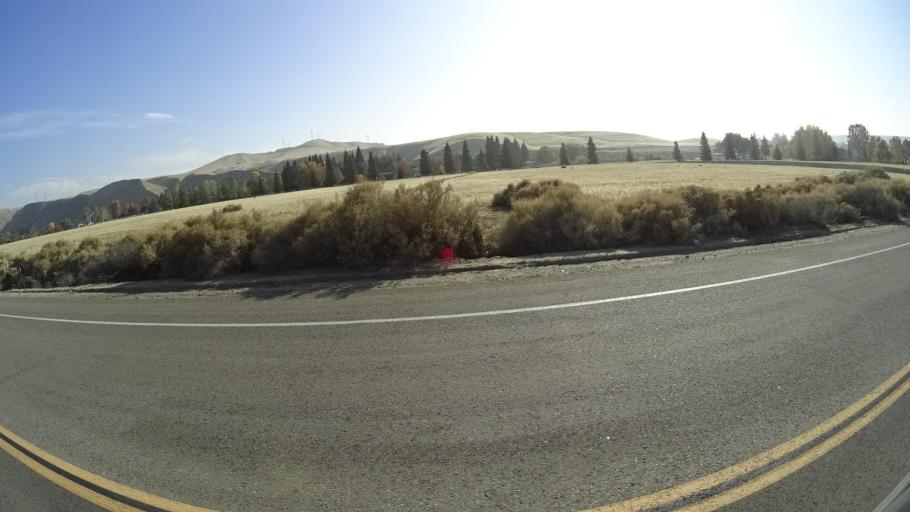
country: US
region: California
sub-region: Kern County
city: Oildale
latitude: 35.4511
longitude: -118.9286
